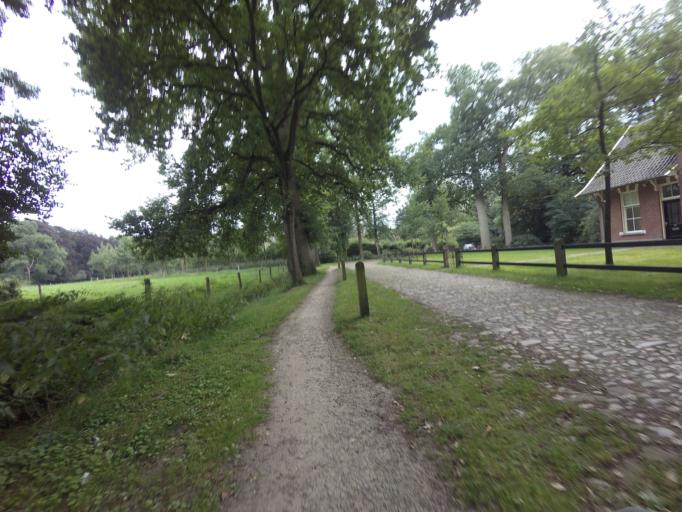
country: DE
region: Lower Saxony
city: Lage
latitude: 52.4713
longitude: 6.9634
